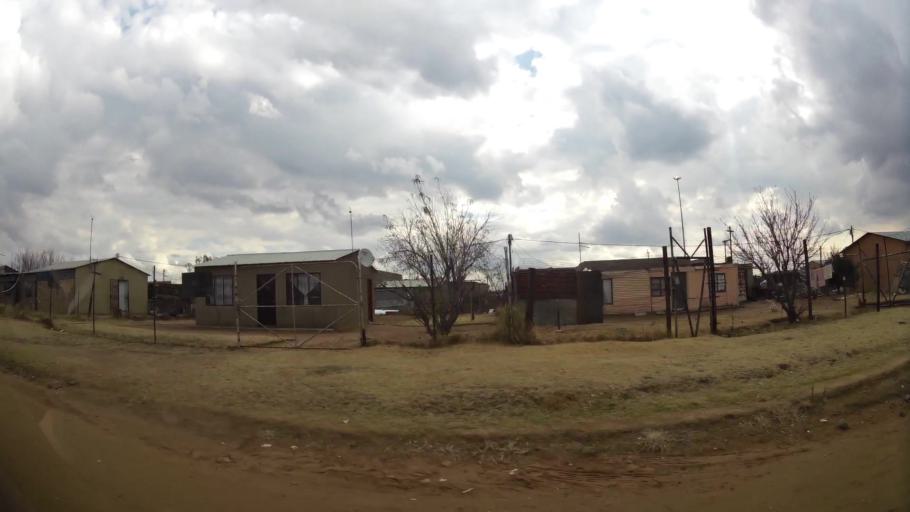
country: ZA
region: Orange Free State
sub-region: Fezile Dabi District Municipality
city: Sasolburg
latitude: -26.8618
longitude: 27.8651
